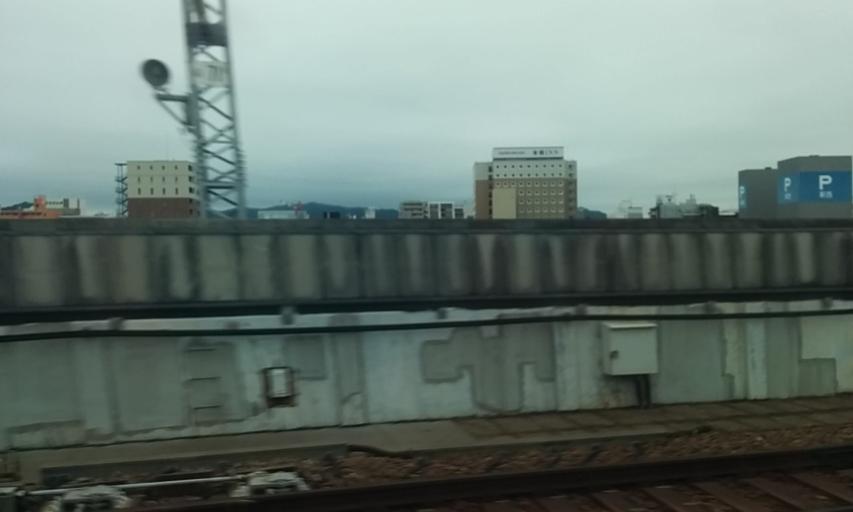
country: JP
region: Hyogo
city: Himeji
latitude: 34.8268
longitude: 134.6865
